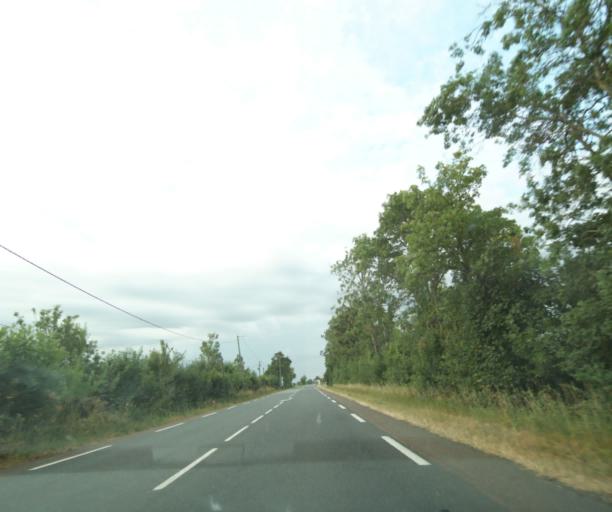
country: FR
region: Poitou-Charentes
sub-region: Departement de la Charente-Maritime
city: Marans
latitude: 46.3495
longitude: -0.9958
